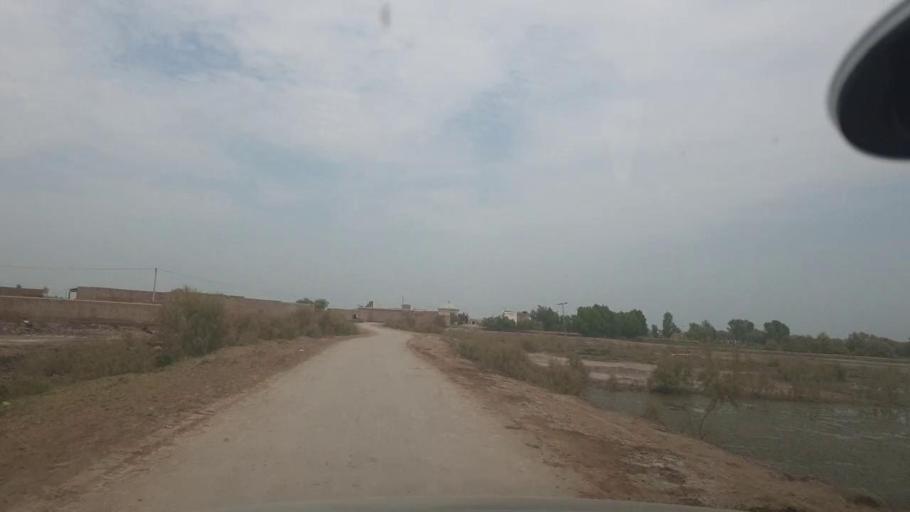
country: PK
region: Balochistan
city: Mehrabpur
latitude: 28.0580
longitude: 68.1500
